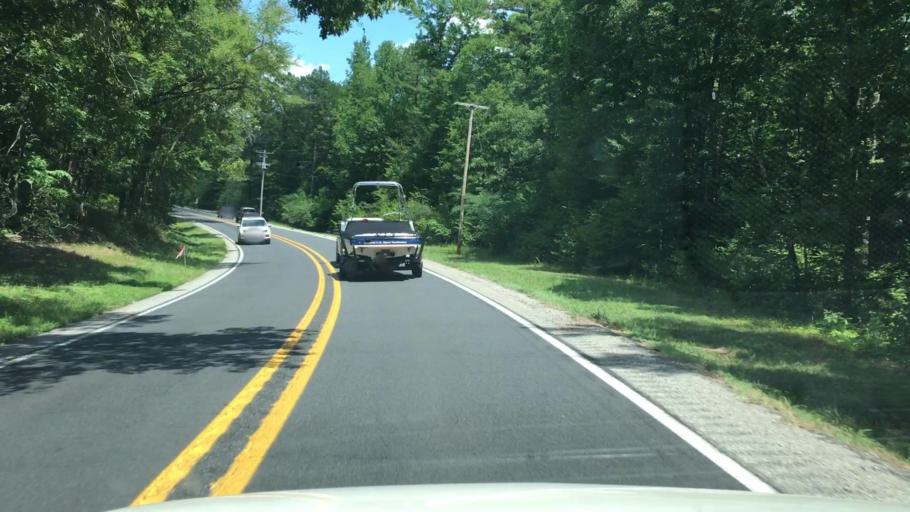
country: US
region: Arkansas
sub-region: Garland County
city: Lake Hamilton
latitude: 34.3850
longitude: -93.1273
